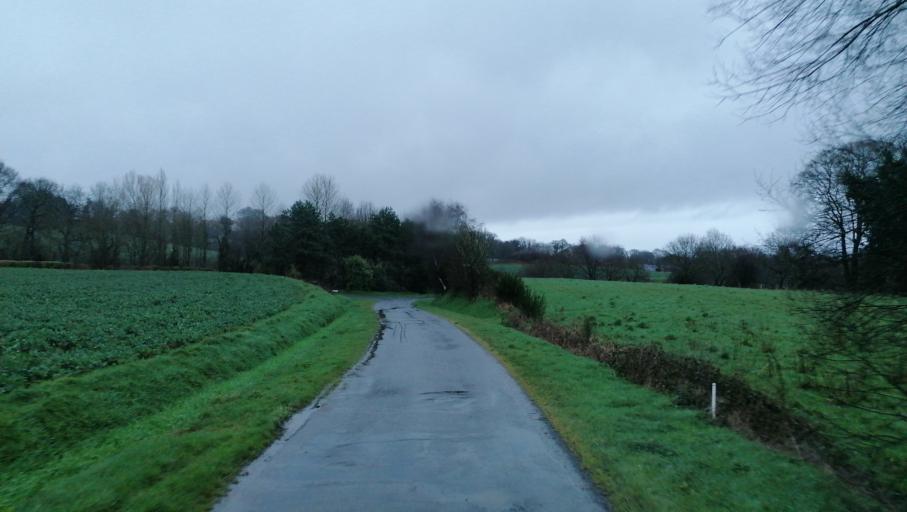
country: FR
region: Brittany
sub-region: Departement des Cotes-d'Armor
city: Plouagat
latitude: 48.4757
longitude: -2.9808
